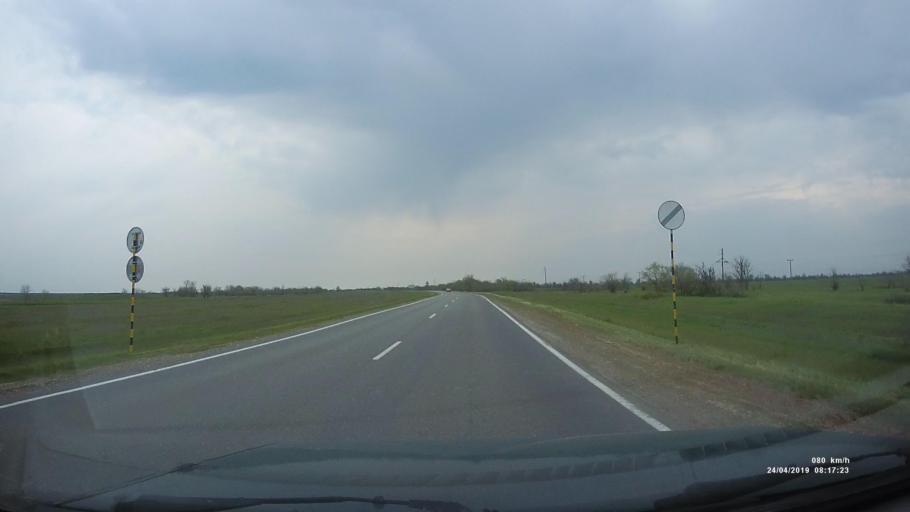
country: RU
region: Kalmykiya
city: Priyutnoye
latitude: 46.0979
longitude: 43.6289
